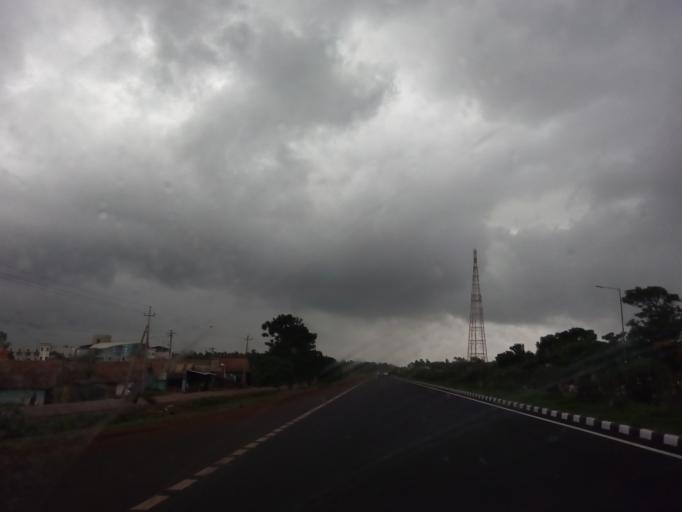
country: IN
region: Karnataka
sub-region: Belgaum
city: Belgaum
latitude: 16.0197
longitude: 74.5203
